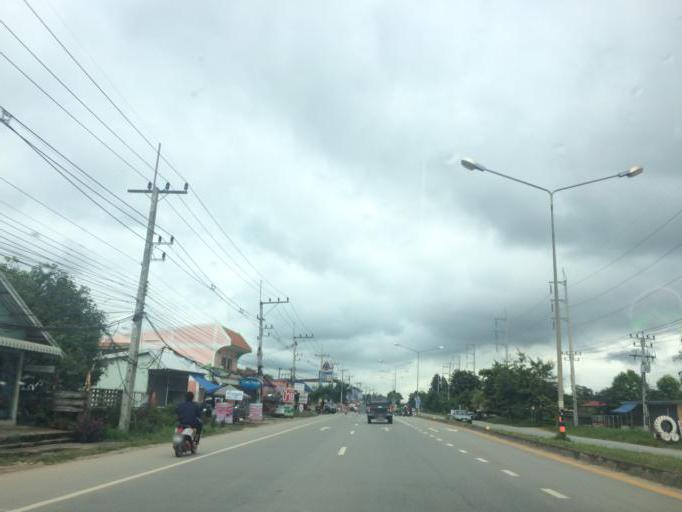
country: TH
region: Chiang Rai
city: Mae Chan
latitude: 20.0542
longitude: 99.8755
